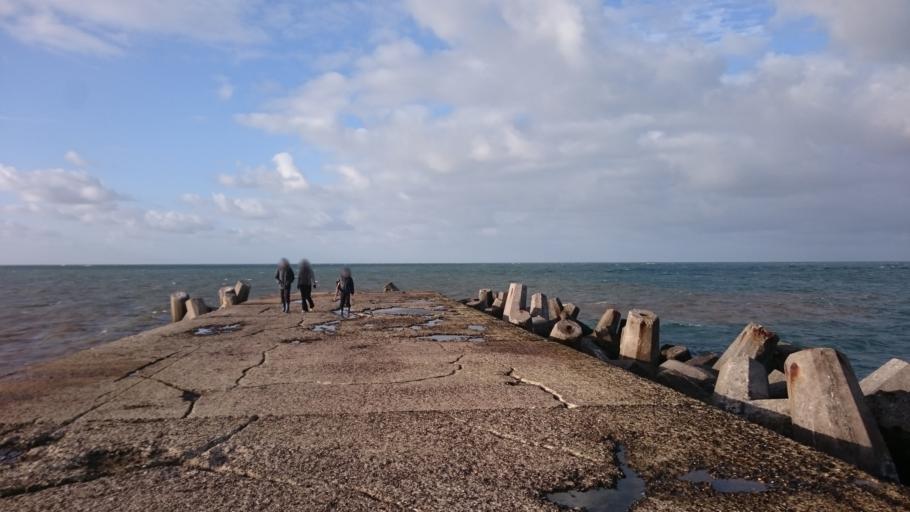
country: DE
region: Schleswig-Holstein
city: Helgoland
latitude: 54.1893
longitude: 7.8836
